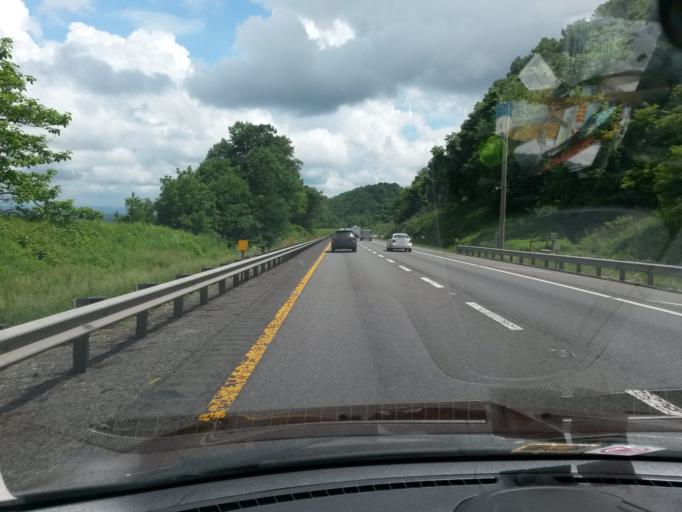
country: US
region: Virginia
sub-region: Carroll County
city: Cana
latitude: 36.6084
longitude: -80.7376
